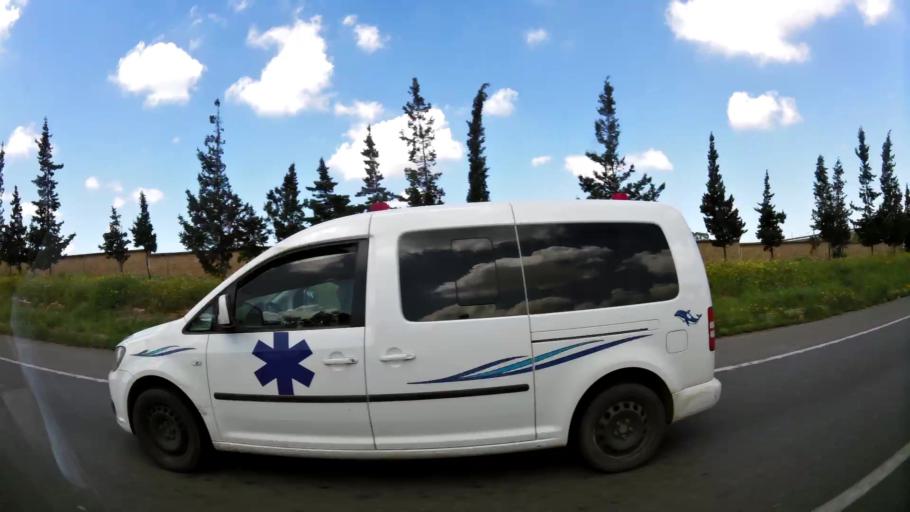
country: MA
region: Grand Casablanca
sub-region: Casablanca
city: Casablanca
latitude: 33.5185
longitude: -7.5835
